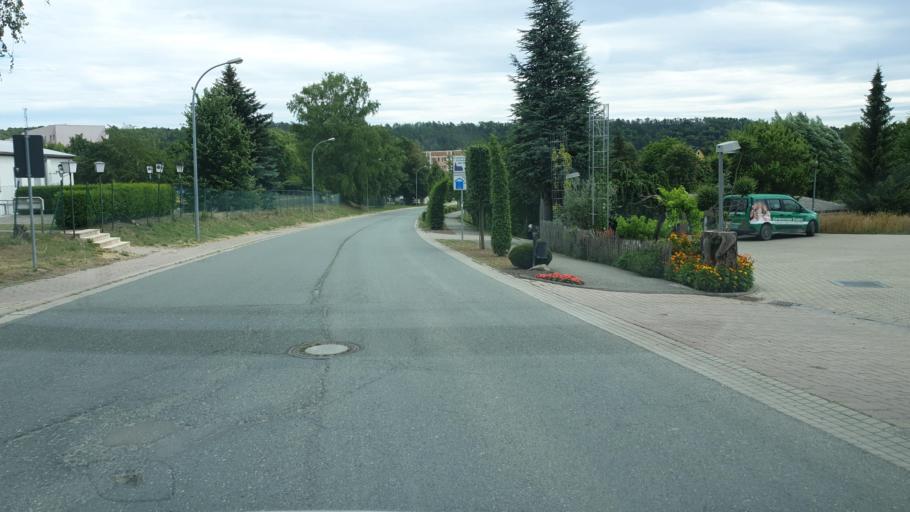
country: DE
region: Saxony-Anhalt
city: Freyburg
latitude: 51.2215
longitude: 11.7642
